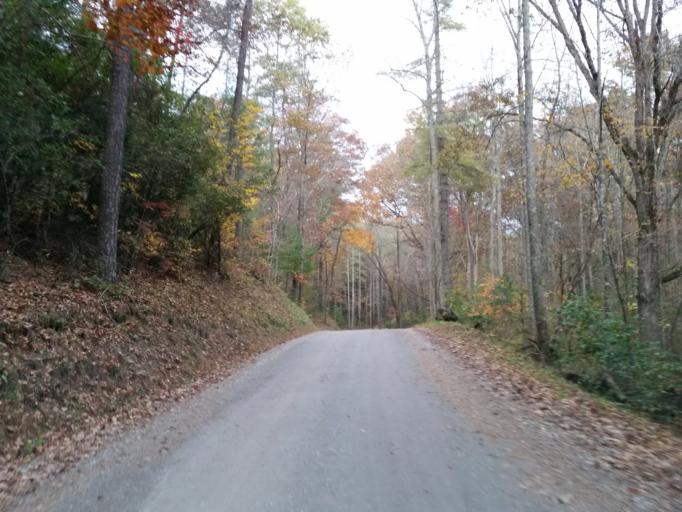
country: US
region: Georgia
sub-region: Fannin County
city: Blue Ridge
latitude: 34.7268
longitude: -84.2092
